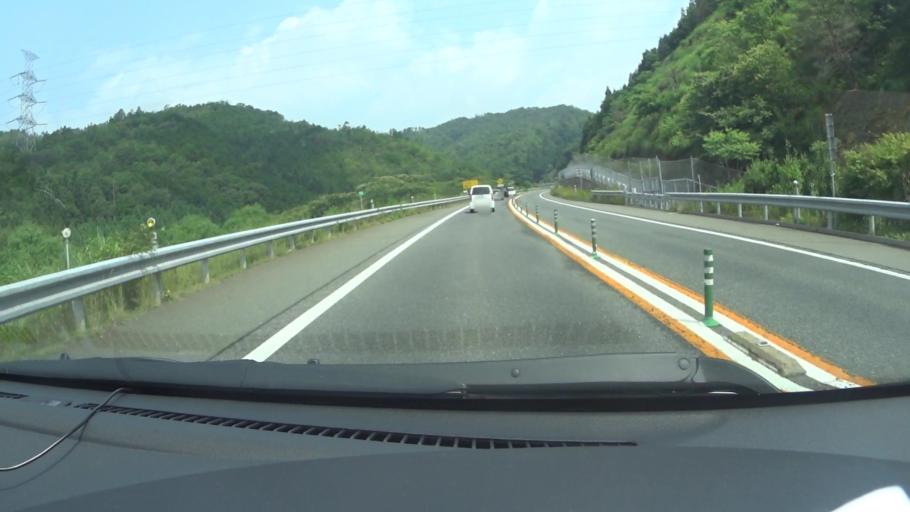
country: JP
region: Kyoto
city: Kameoka
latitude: 35.1306
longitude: 135.4579
